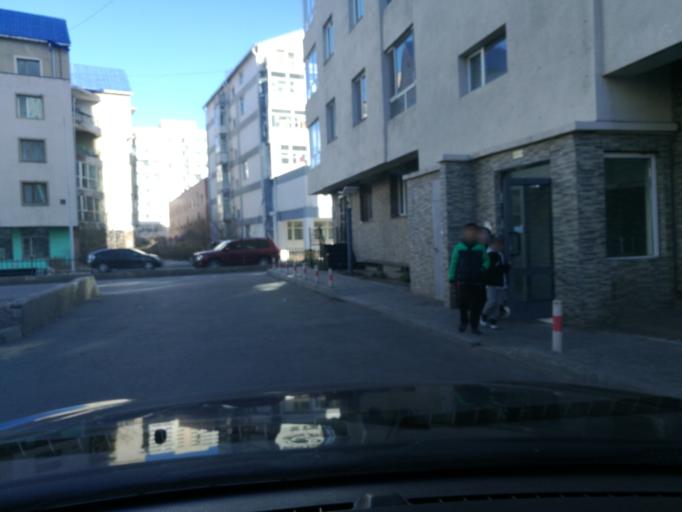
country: MN
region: Ulaanbaatar
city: Ulaanbaatar
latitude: 47.8901
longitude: 106.9000
